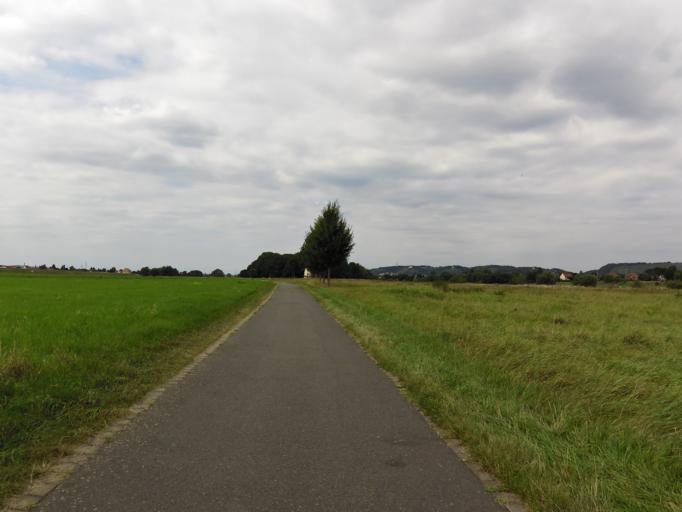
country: DE
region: Saxony
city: Radebeul
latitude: 51.0868
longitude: 13.6620
